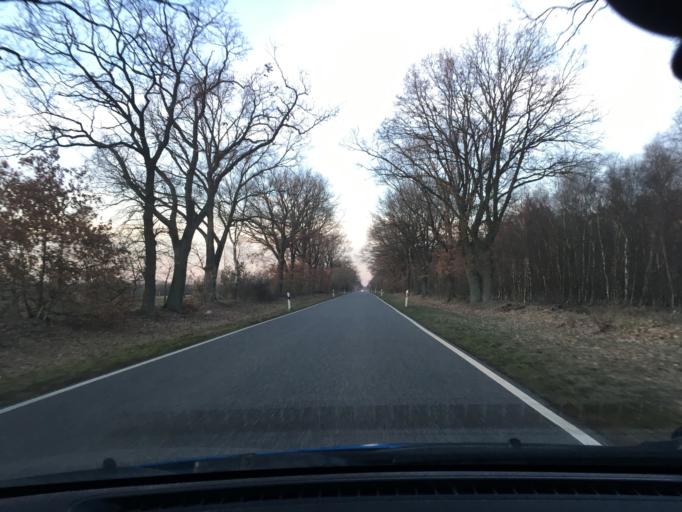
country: DE
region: Schleswig-Holstein
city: Langenlehsten
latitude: 53.5089
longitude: 10.7430
